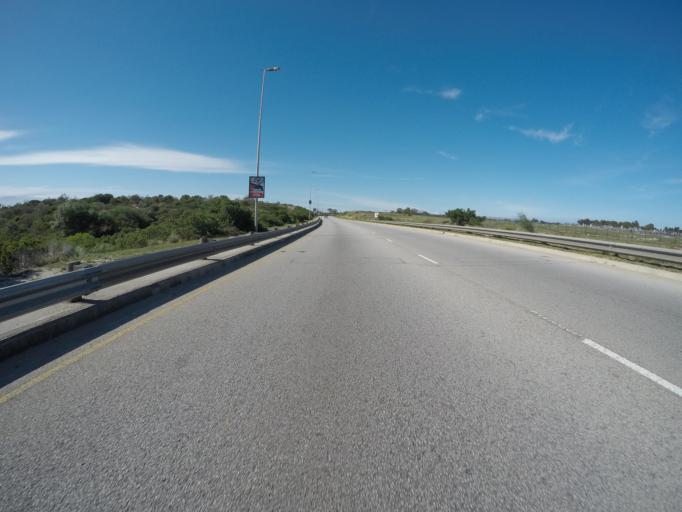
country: ZA
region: Eastern Cape
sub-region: Nelson Mandela Bay Metropolitan Municipality
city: Port Elizabeth
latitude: -33.9854
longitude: 25.6409
